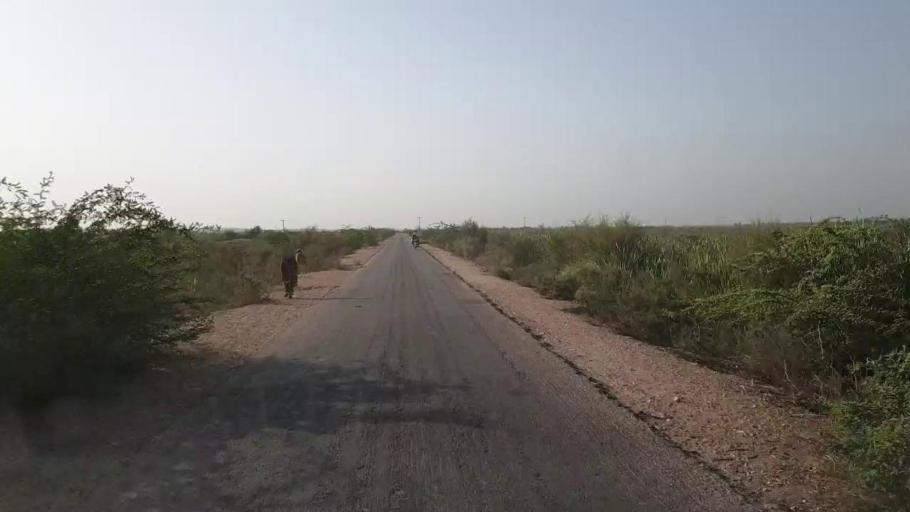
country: PK
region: Sindh
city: Jam Sahib
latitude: 26.4494
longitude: 68.8631
